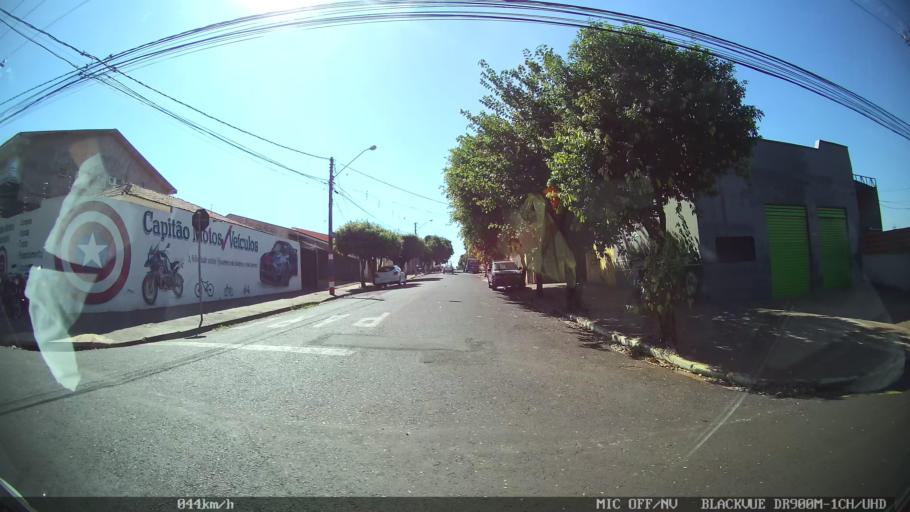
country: BR
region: Sao Paulo
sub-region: Sao Jose Do Rio Preto
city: Sao Jose do Rio Preto
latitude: -20.7766
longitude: -49.3835
